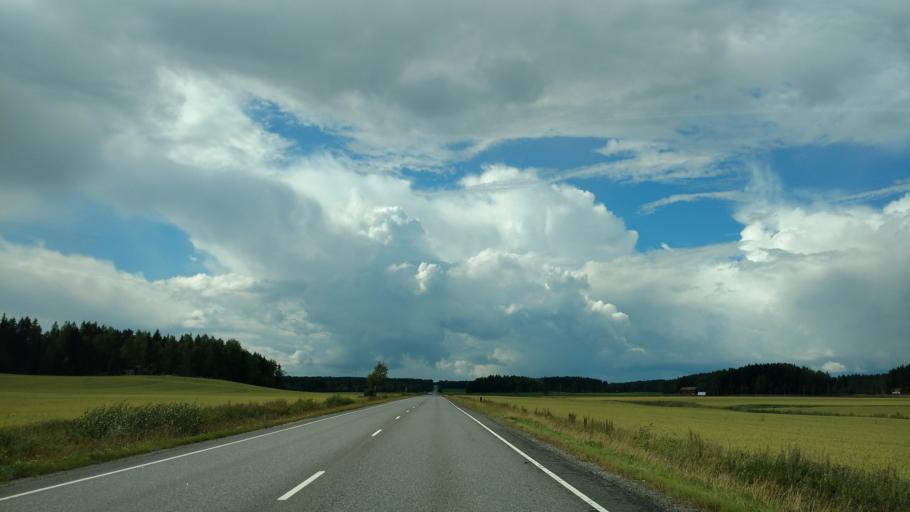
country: FI
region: Varsinais-Suomi
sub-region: Turku
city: Sauvo
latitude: 60.3900
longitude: 22.8724
